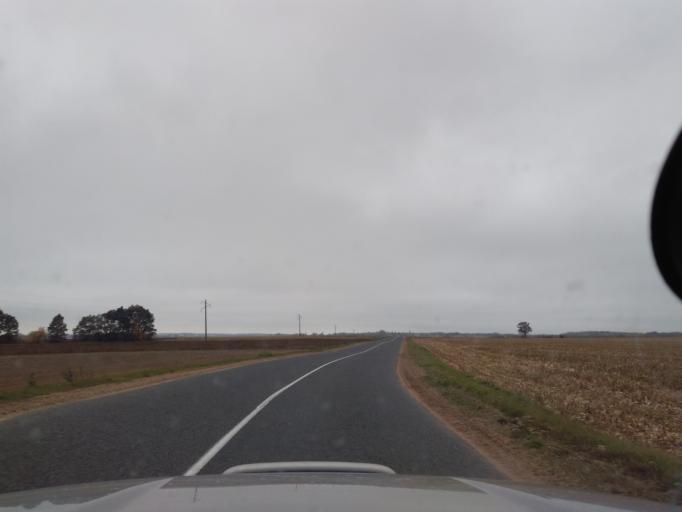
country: BY
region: Minsk
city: Kapyl'
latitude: 53.1498
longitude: 27.1939
